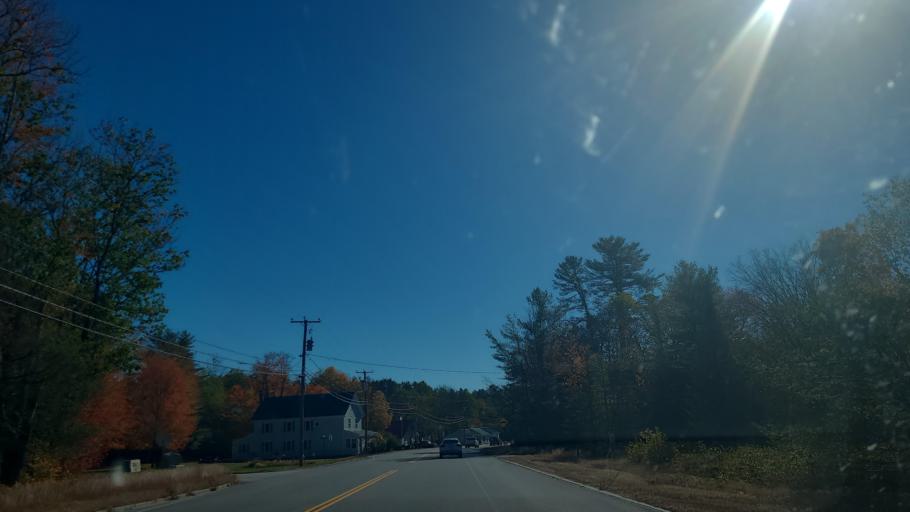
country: US
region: New Hampshire
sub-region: Carroll County
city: Conway
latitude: 44.0147
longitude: -71.1028
